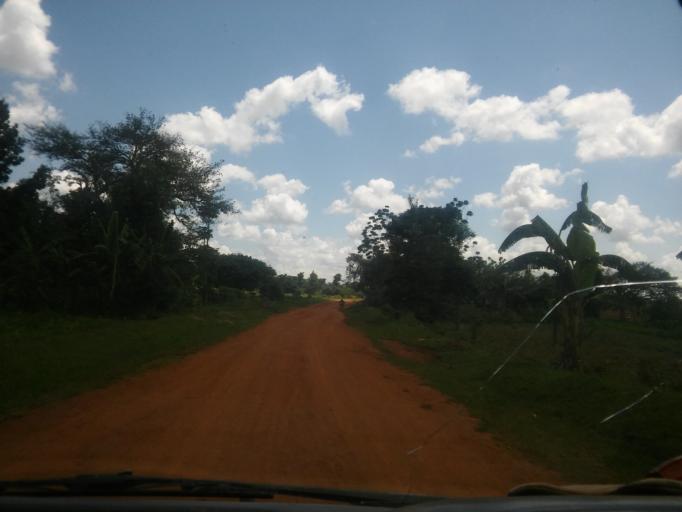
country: UG
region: Eastern Region
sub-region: Budaka District
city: Budaka
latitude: 1.1118
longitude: 33.9592
